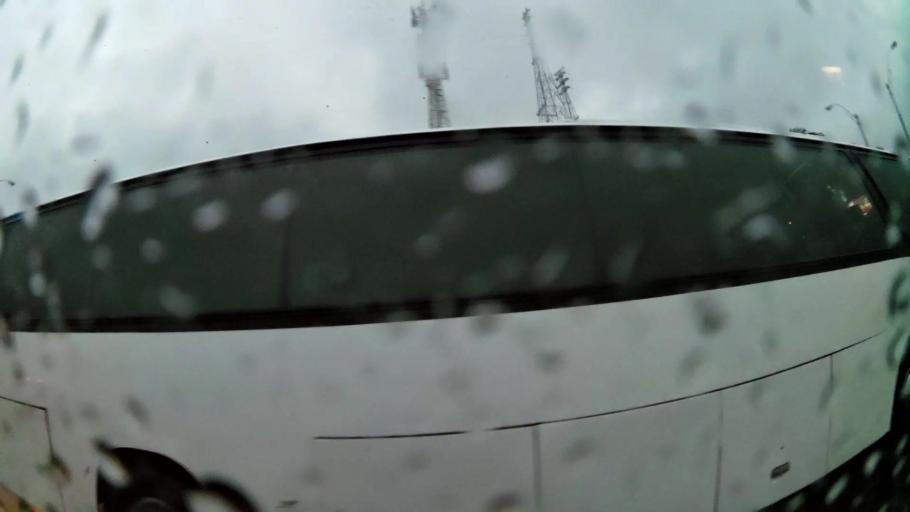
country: PA
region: Panama
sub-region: Distrito de Panama
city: Paraiso
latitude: 9.0353
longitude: -79.6314
